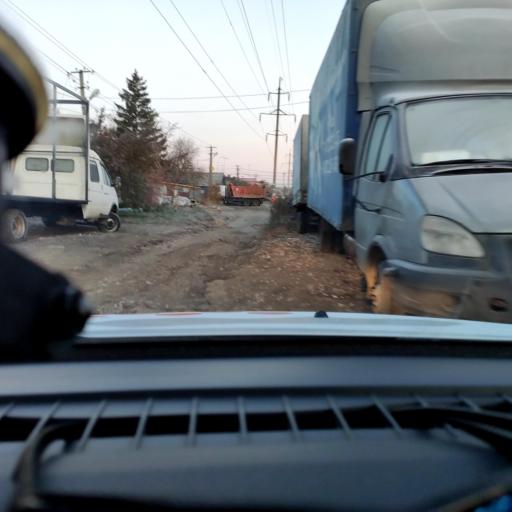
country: RU
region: Samara
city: Samara
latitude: 53.1756
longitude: 50.1821
